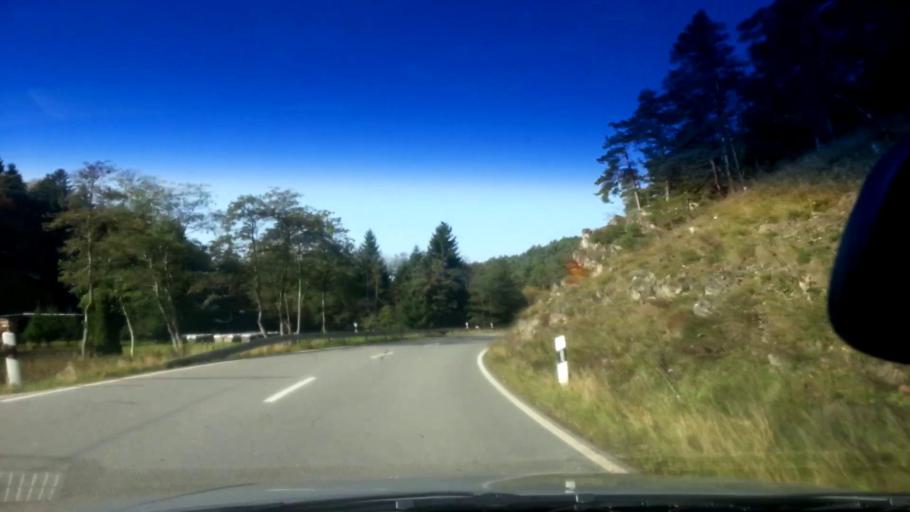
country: DE
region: Bavaria
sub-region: Upper Franconia
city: Stadelhofen
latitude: 49.9679
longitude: 11.1958
